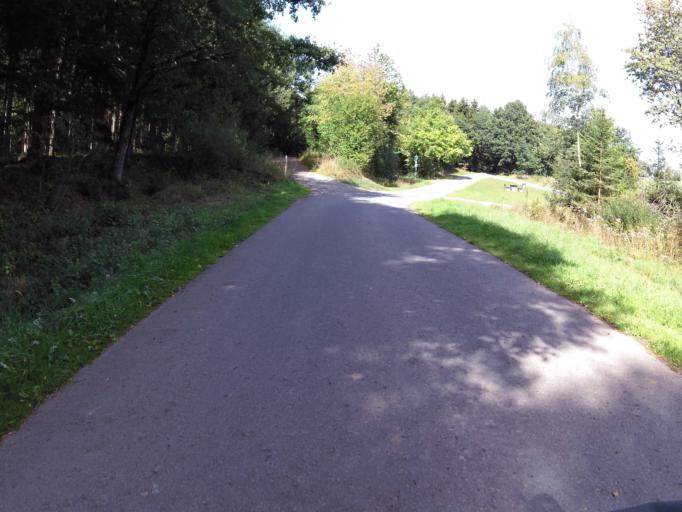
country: DE
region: Rheinland-Pfalz
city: Arzfeld
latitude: 50.0956
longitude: 6.2715
